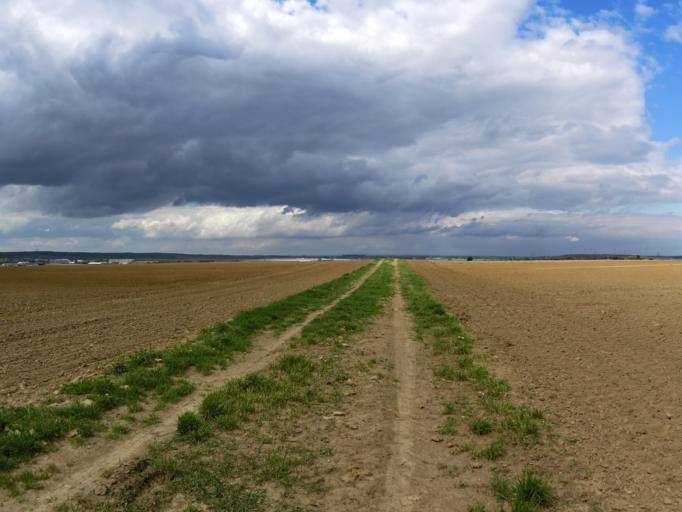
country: DE
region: Bavaria
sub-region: Regierungsbezirk Unterfranken
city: Oberpleichfeld
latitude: 49.8548
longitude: 10.0803
